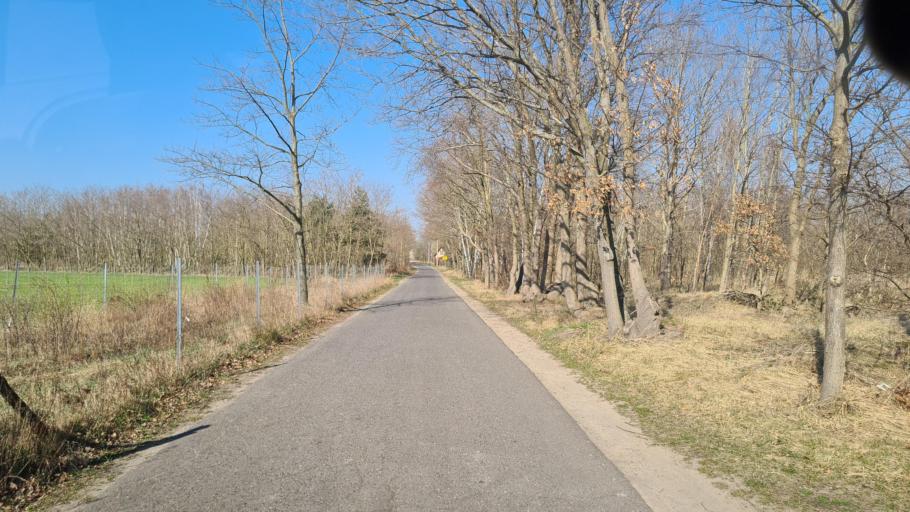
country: DE
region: Brandenburg
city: Calau
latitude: 51.7969
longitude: 13.9813
